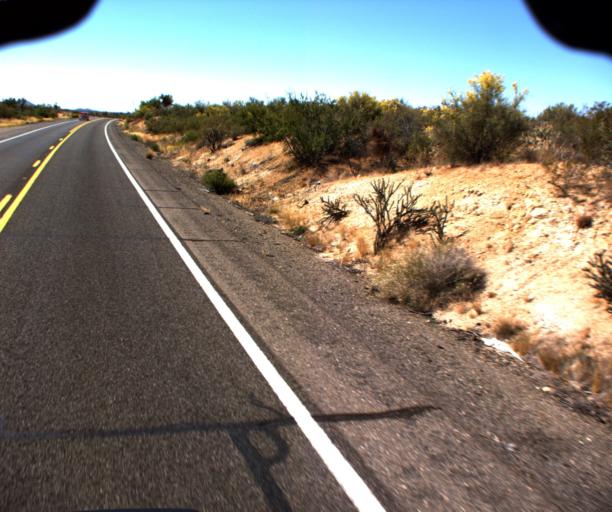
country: US
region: Arizona
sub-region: Yavapai County
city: Congress
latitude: 34.2312
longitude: -113.0708
